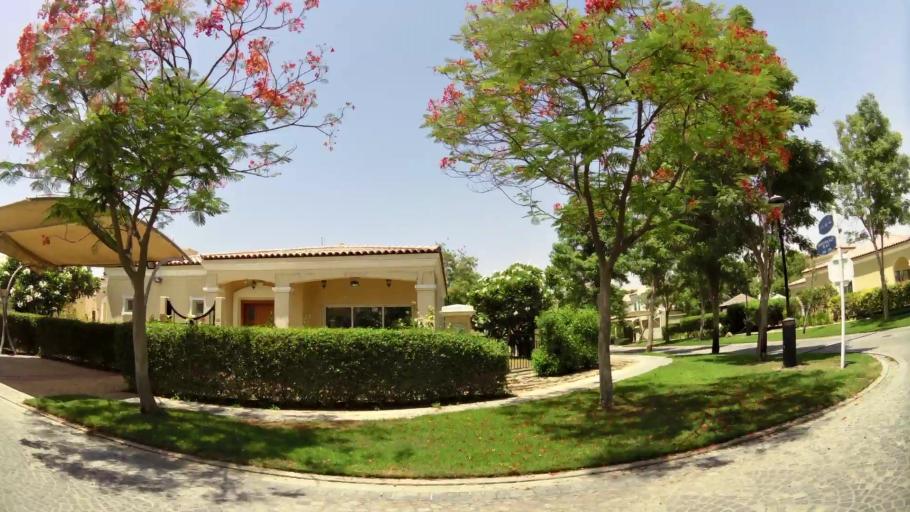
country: AE
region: Dubai
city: Dubai
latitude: 25.0001
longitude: 55.1647
